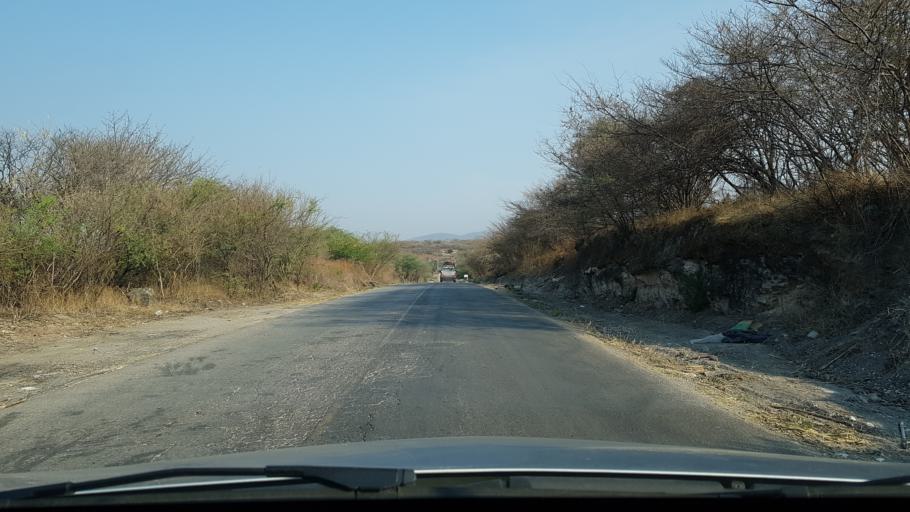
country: MX
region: Morelos
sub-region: Tlaltizapan de Zapata
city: Colonia Palo Prieto (Chipitongo)
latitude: 18.6893
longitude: -99.0943
